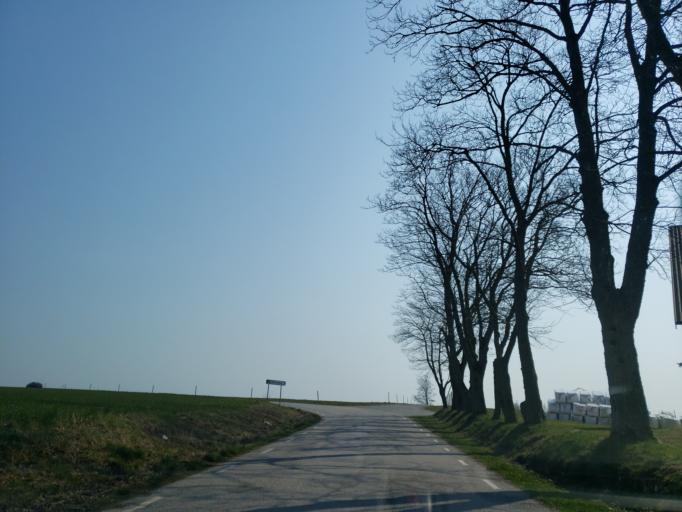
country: SE
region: Skane
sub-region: Simrishamns Kommun
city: Simrishamn
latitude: 55.5067
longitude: 14.2991
